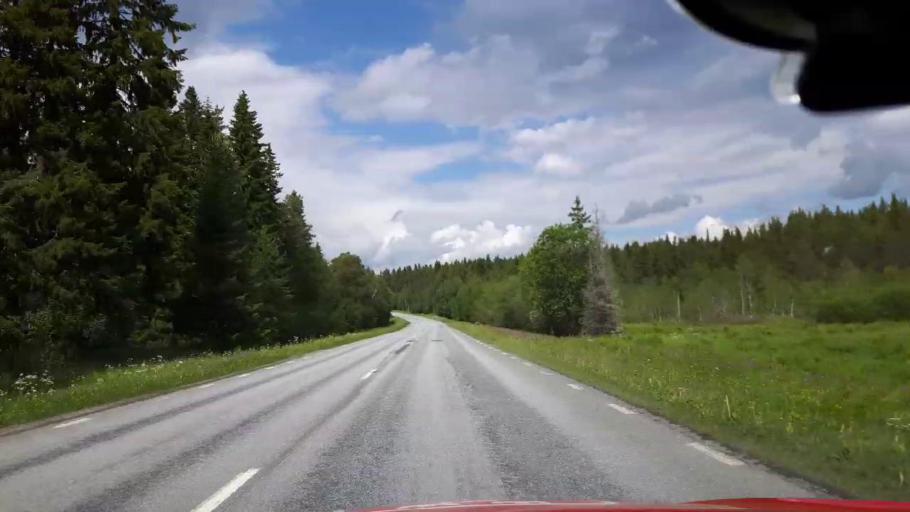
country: SE
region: Jaemtland
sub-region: Krokoms Kommun
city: Krokom
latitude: 63.3742
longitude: 14.3862
